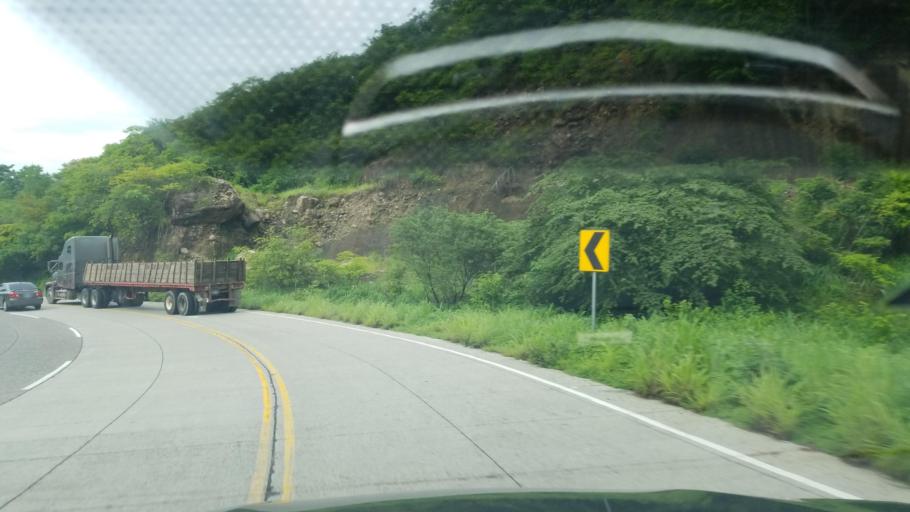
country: HN
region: Francisco Morazan
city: El Porvenir
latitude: 13.7125
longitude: -87.3185
